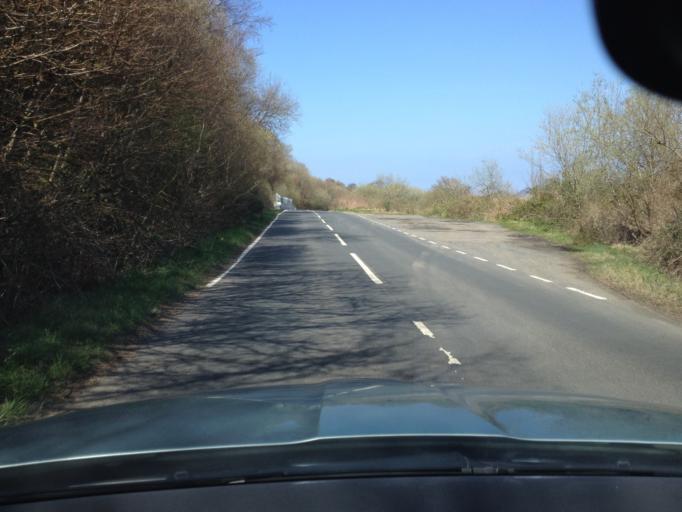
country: GB
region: Scotland
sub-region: North Ayrshire
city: Lamlash
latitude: 55.4607
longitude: -5.0864
